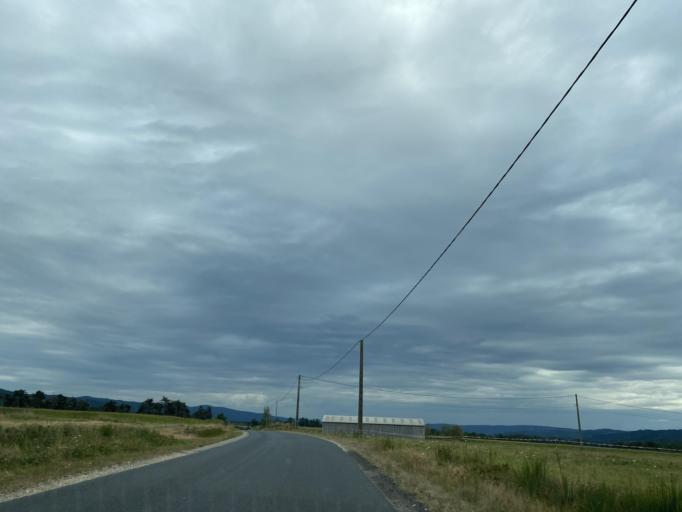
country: FR
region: Auvergne
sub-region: Departement du Puy-de-Dome
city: Ambert
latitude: 45.5268
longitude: 3.7395
